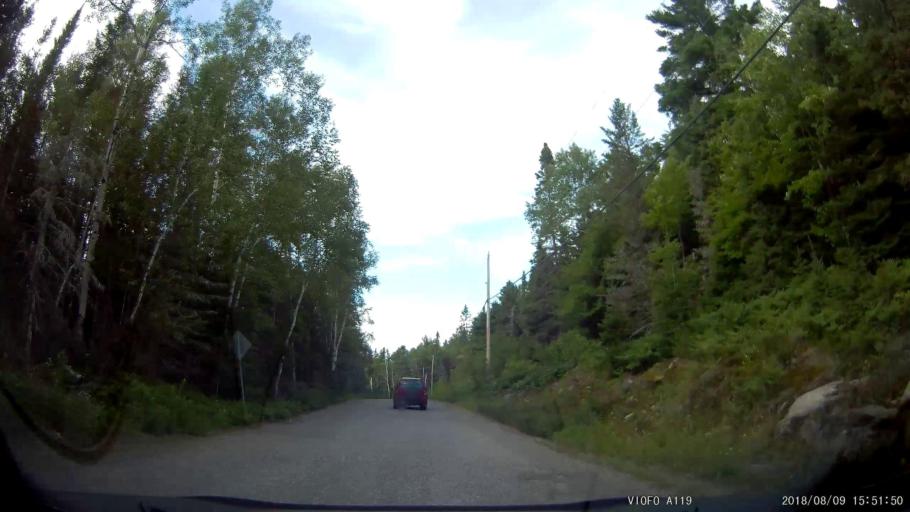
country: CA
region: Ontario
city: Rayside-Balfour
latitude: 46.5958
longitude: -81.5321
